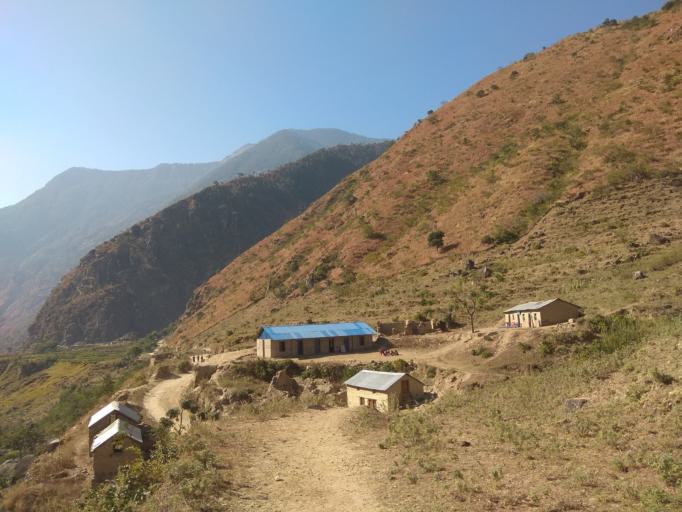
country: NP
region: Far Western
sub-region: Seti Zone
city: Achham
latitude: 29.2213
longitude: 81.6401
